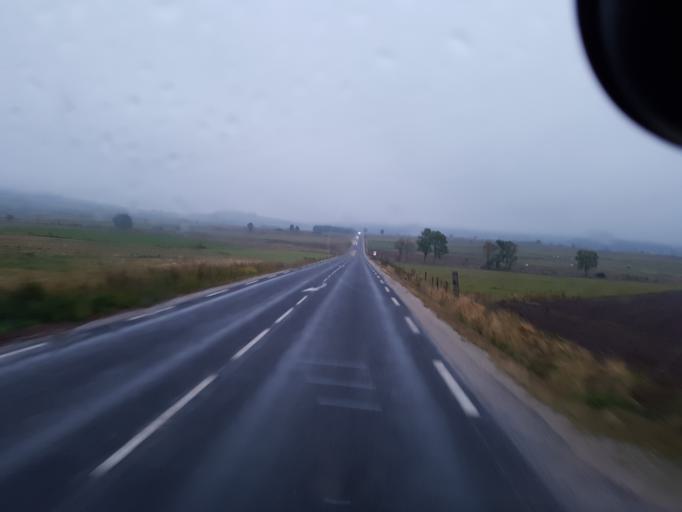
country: FR
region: Languedoc-Roussillon
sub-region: Departement de la Lozere
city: Langogne
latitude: 44.8171
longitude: 3.8738
